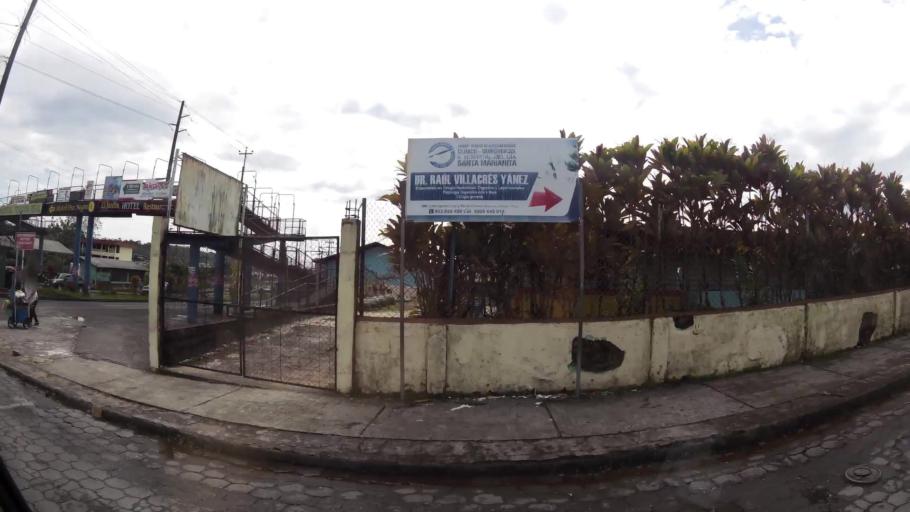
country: EC
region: Pastaza
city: Puyo
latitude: -1.4931
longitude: -77.9998
